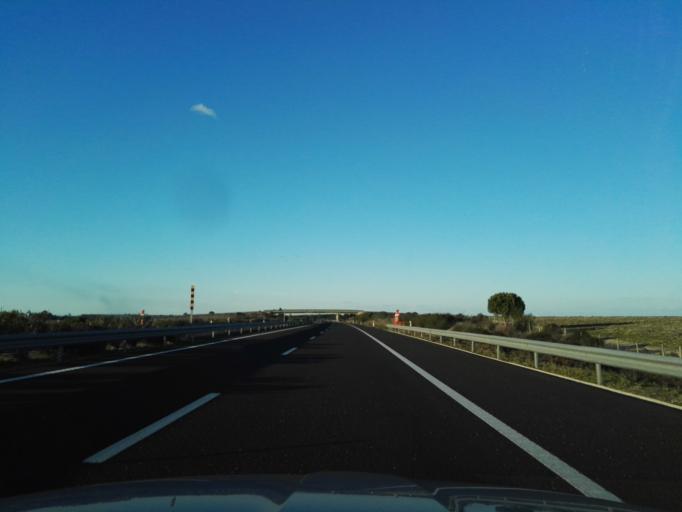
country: PT
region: Santarem
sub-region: Benavente
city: Poceirao
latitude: 38.7718
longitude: -8.6829
